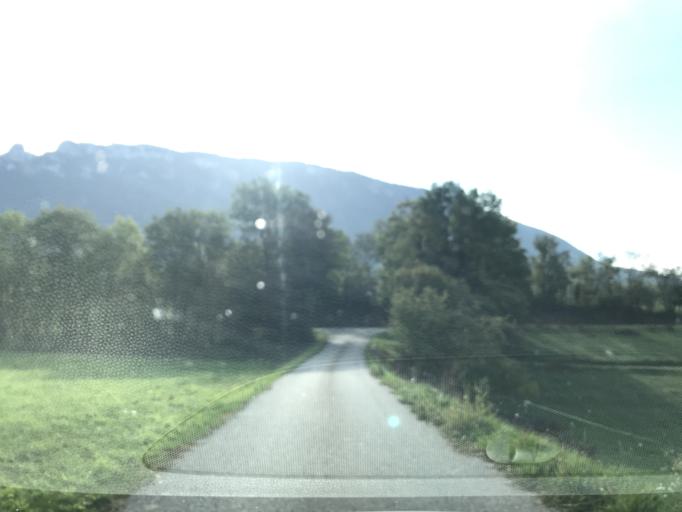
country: FR
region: Rhone-Alpes
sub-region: Departement de la Savoie
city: Yenne
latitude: 45.6854
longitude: 5.7959
